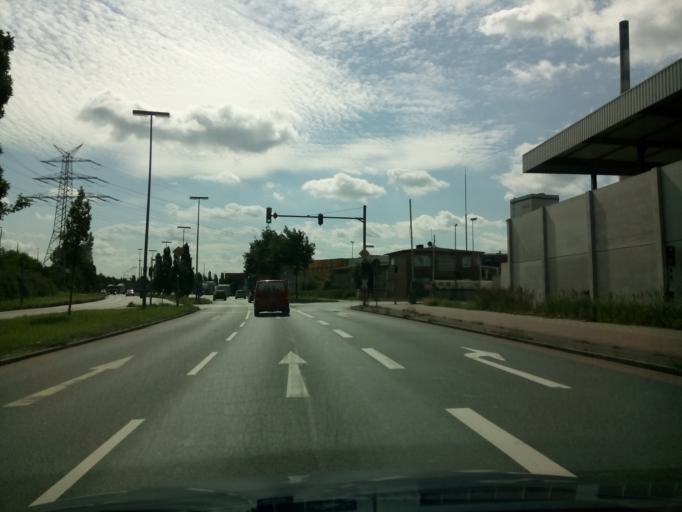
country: DE
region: Lower Saxony
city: Ritterhude
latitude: 53.1296
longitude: 8.7261
